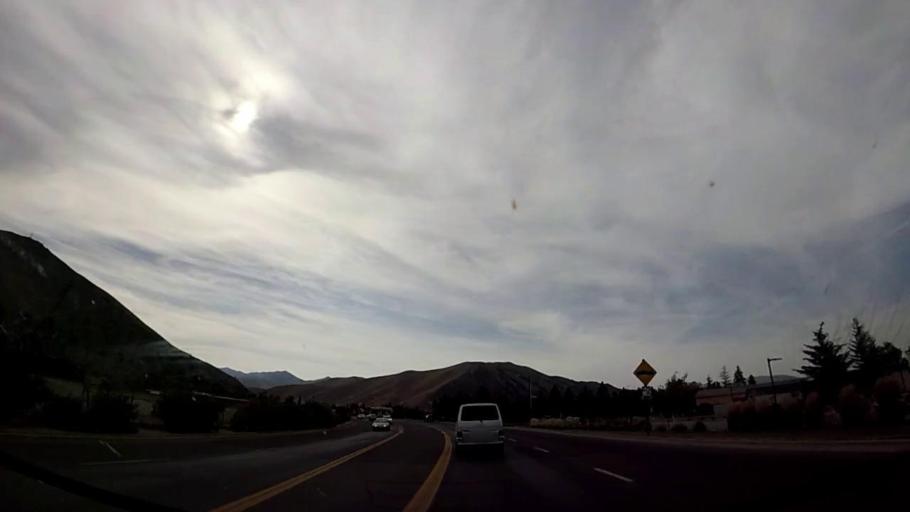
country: US
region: Idaho
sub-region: Blaine County
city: Hailey
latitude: 43.5132
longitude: -114.3036
